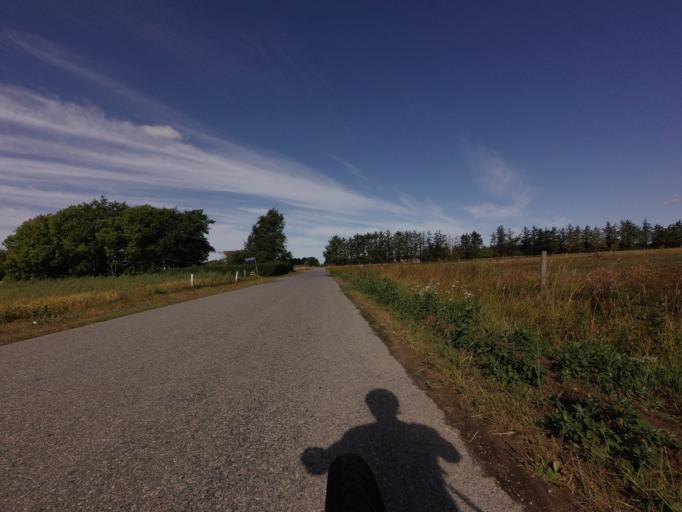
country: DK
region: North Denmark
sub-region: Hjorring Kommune
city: Vra
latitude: 57.3932
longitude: 9.9624
